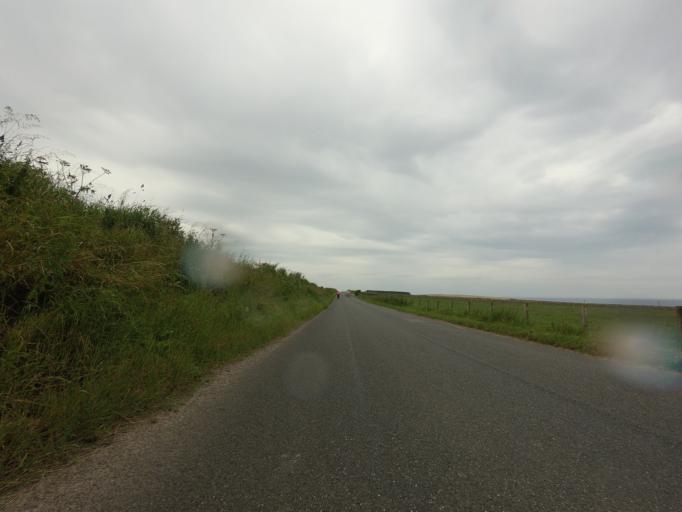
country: GB
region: Scotland
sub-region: Aberdeenshire
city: Whitehills
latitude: 57.6724
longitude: -2.6310
